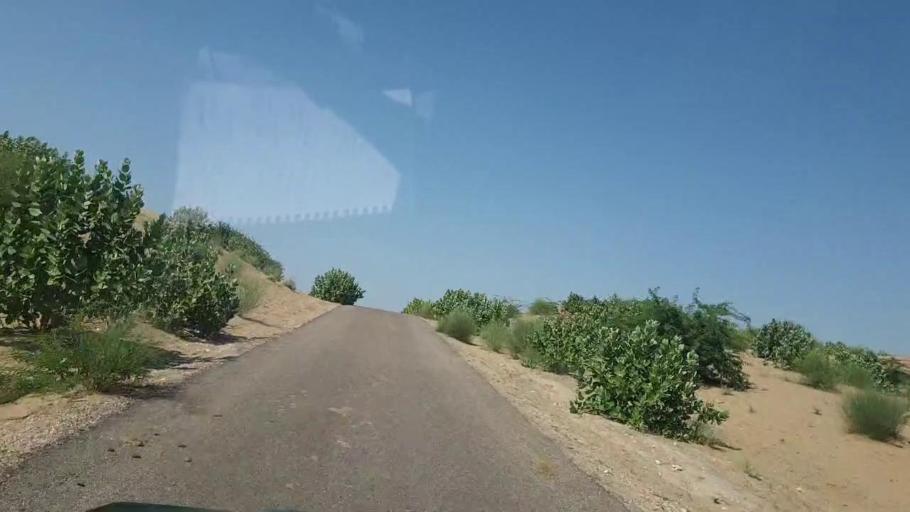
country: PK
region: Sindh
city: Chor
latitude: 25.6202
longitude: 70.3174
